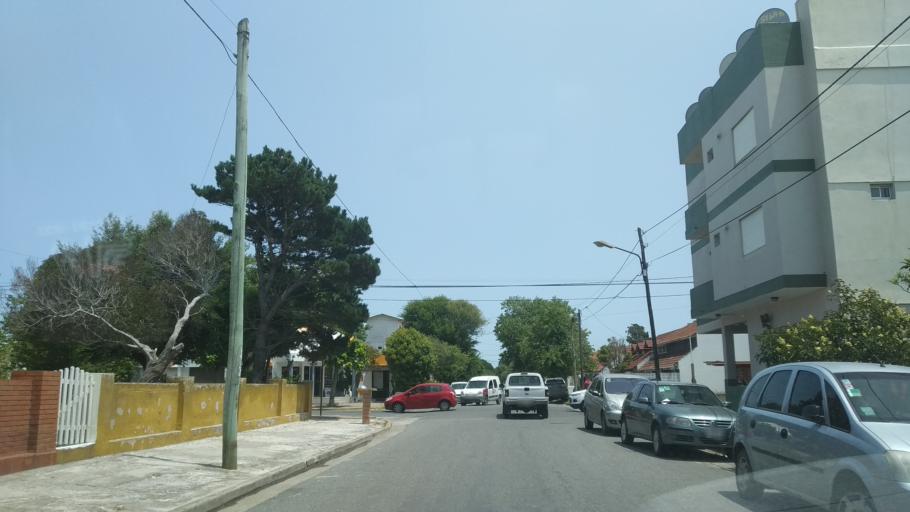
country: AR
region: Buenos Aires
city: Mar del Tuyu
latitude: -36.5601
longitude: -56.6907
